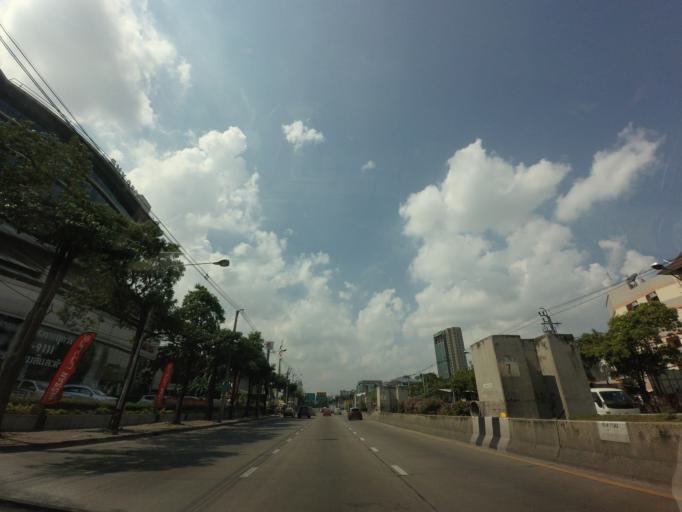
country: TH
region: Bangkok
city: Chatuchak
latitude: 13.8405
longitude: 100.5820
